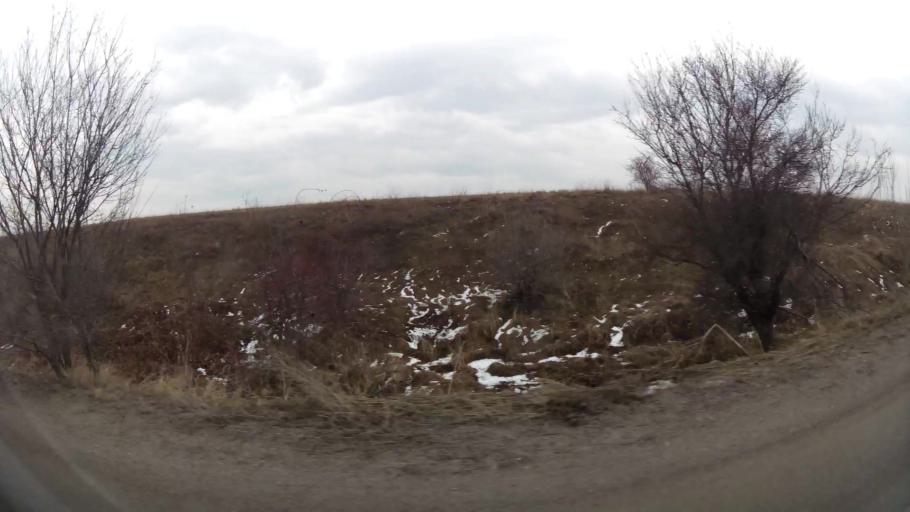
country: BG
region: Sofiya
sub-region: Obshtina Bozhurishte
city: Bozhurishte
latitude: 42.7014
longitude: 23.2207
